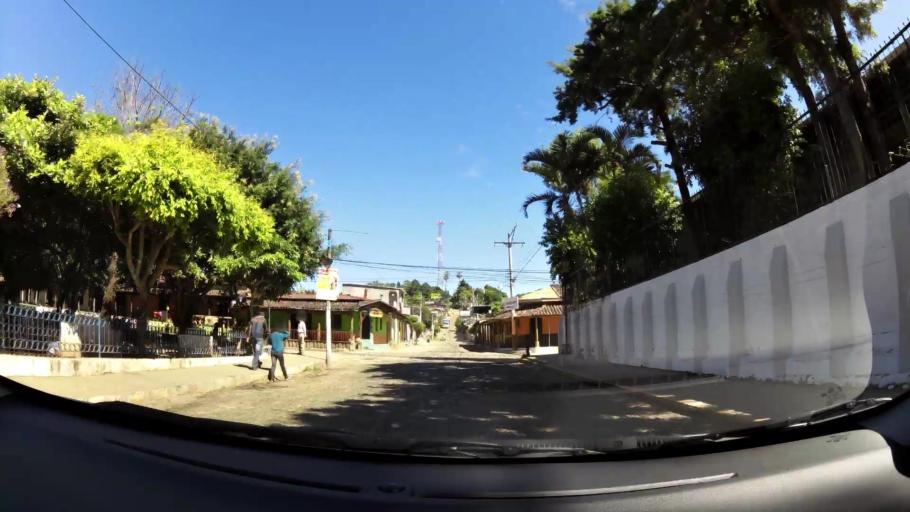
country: SV
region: Ahuachapan
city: Concepcion de Ataco
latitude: 13.8704
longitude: -89.8503
